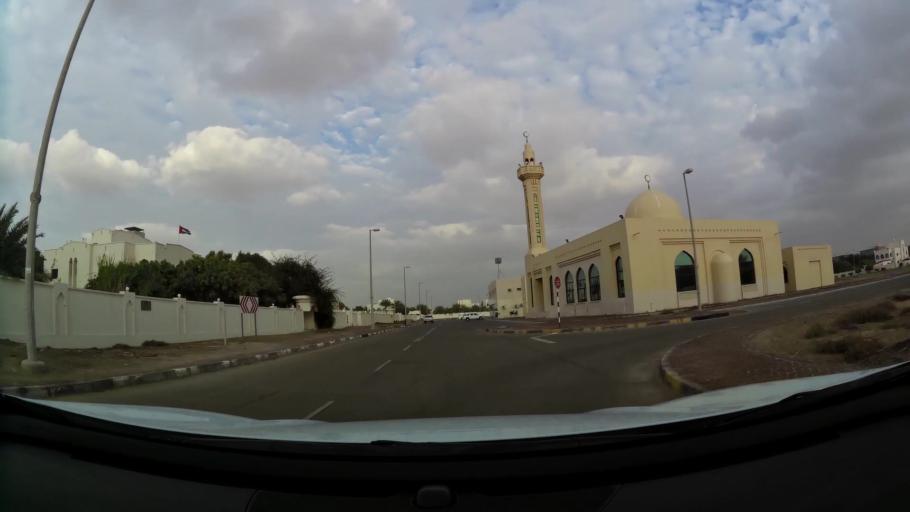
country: AE
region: Abu Dhabi
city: Abu Dhabi
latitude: 24.3815
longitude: 54.5306
